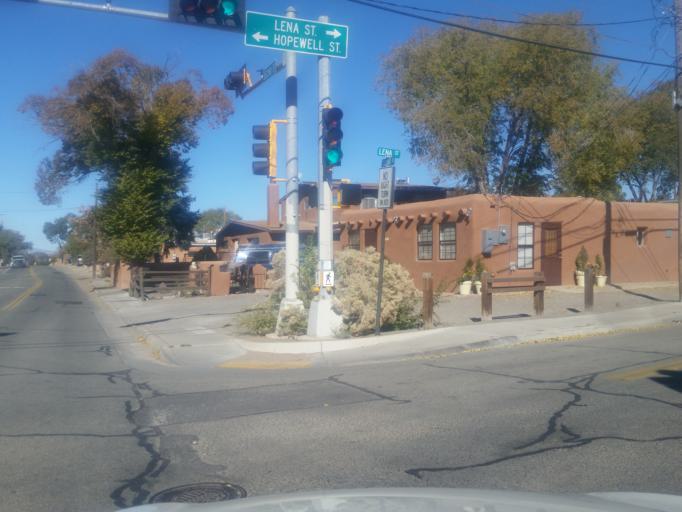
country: US
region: New Mexico
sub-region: Santa Fe County
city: Santa Fe
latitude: 35.6633
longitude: -105.9658
